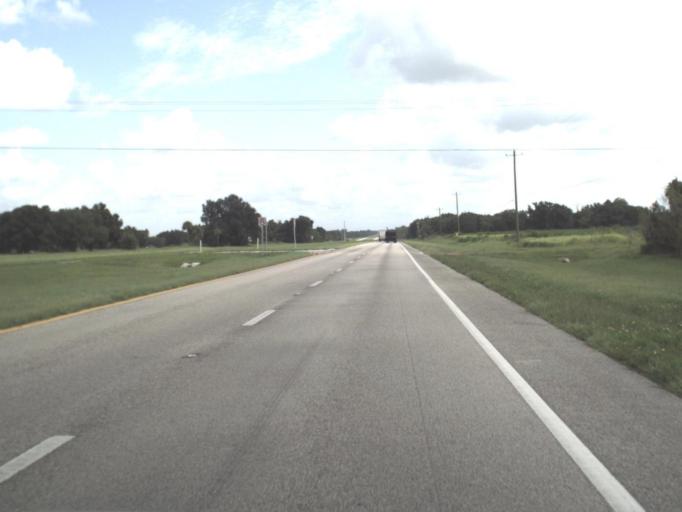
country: US
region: Florida
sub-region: DeSoto County
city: Arcadia
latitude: 27.3014
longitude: -81.8222
